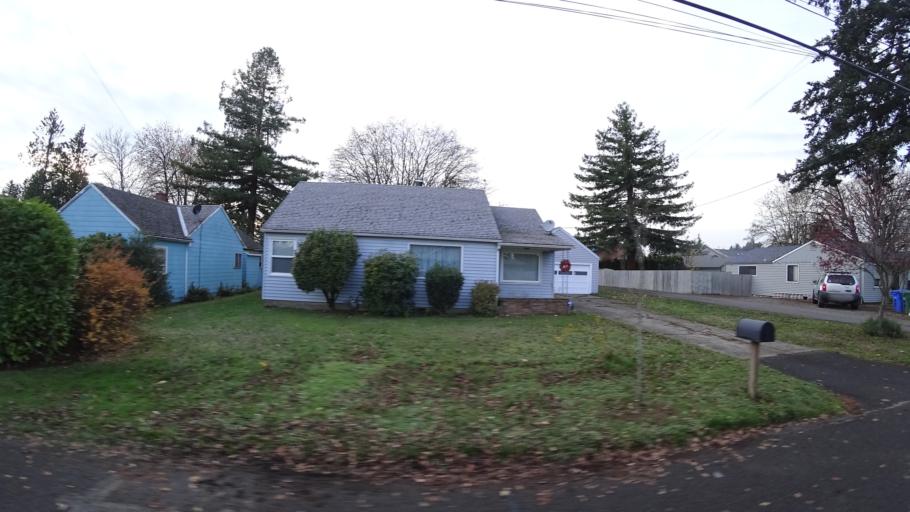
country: US
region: Oregon
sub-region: Multnomah County
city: Lents
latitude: 45.5166
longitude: -122.5185
